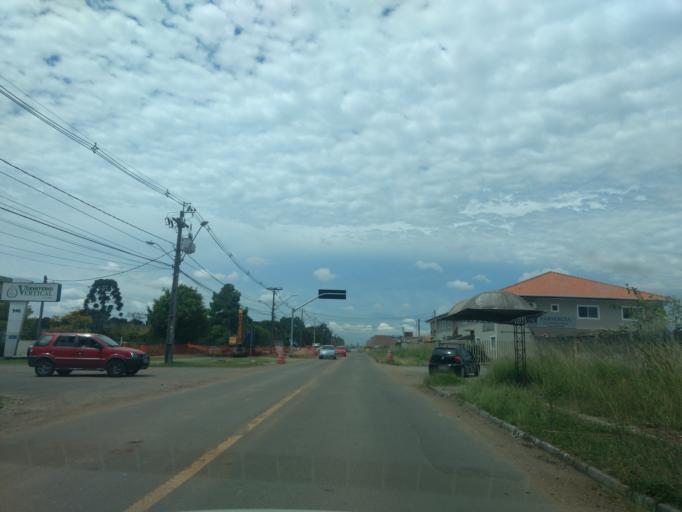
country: BR
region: Parana
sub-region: Pinhais
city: Pinhais
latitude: -25.4217
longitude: -49.2170
